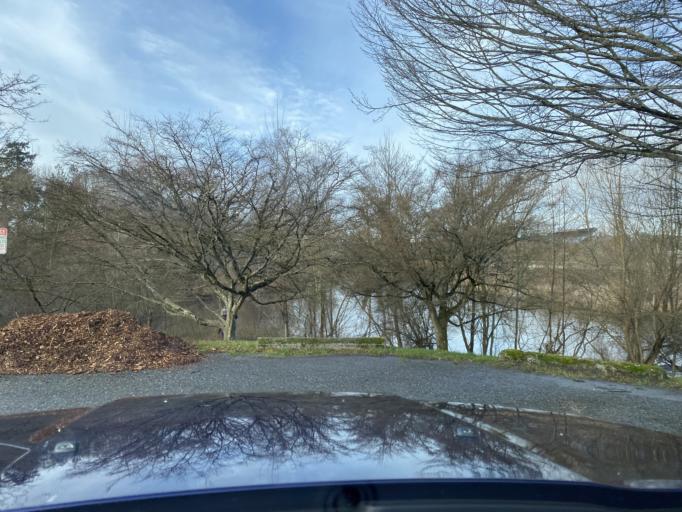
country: US
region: Washington
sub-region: King County
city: Seattle
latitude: 47.6415
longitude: -122.2928
